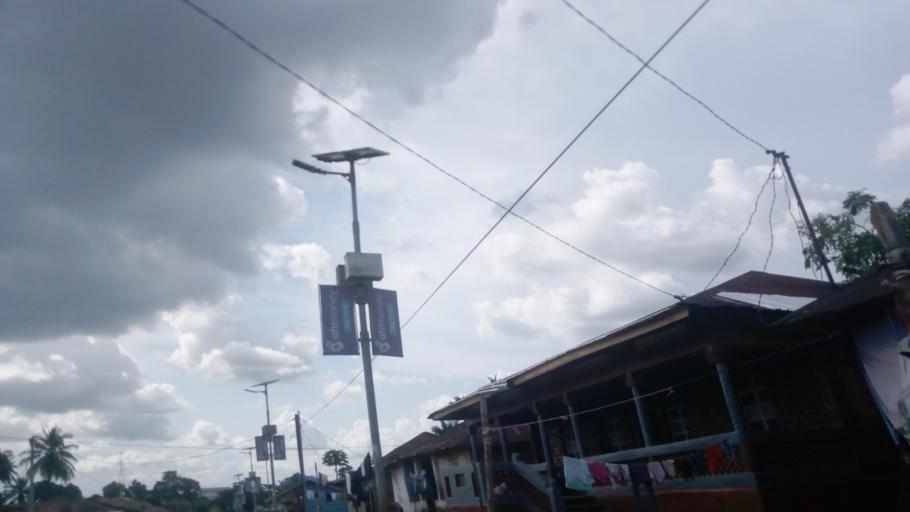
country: SL
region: Northern Province
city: Makeni
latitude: 8.8910
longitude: -12.0453
